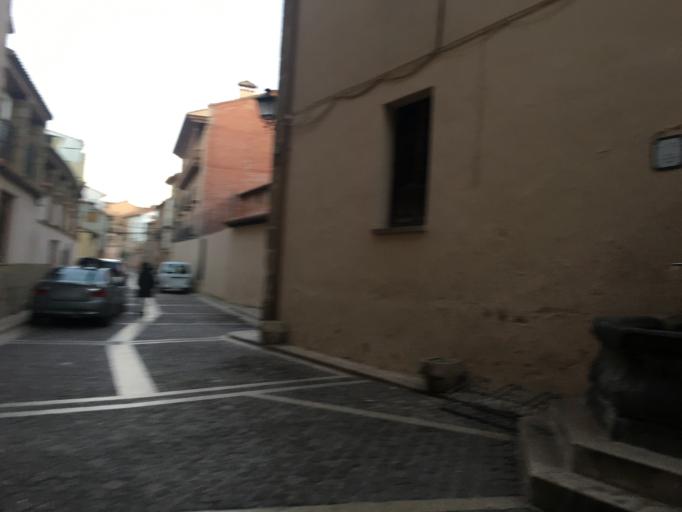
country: ES
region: Aragon
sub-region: Provincia de Teruel
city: Mora de Rubielos
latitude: 40.2517
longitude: -0.7530
